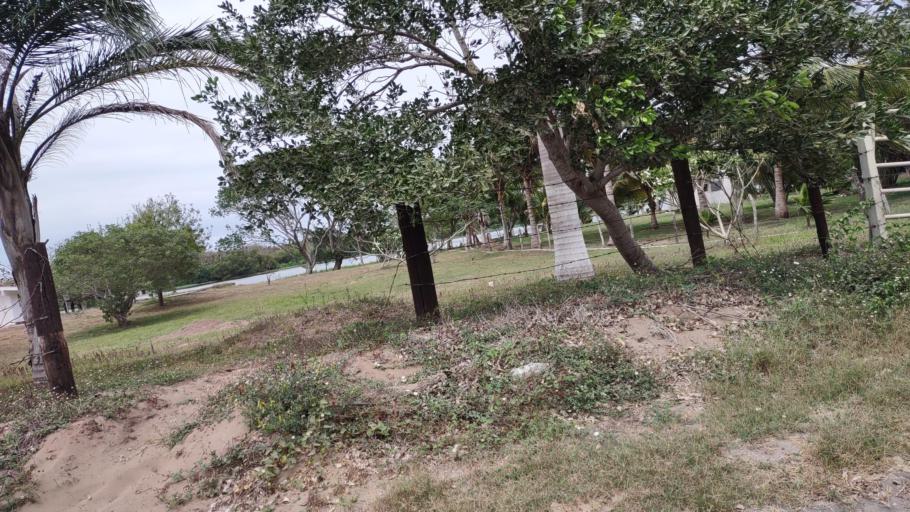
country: MX
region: Veracruz
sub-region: La Antigua
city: Nicolas Blanco (San Pancho)
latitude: 19.3105
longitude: -96.3031
